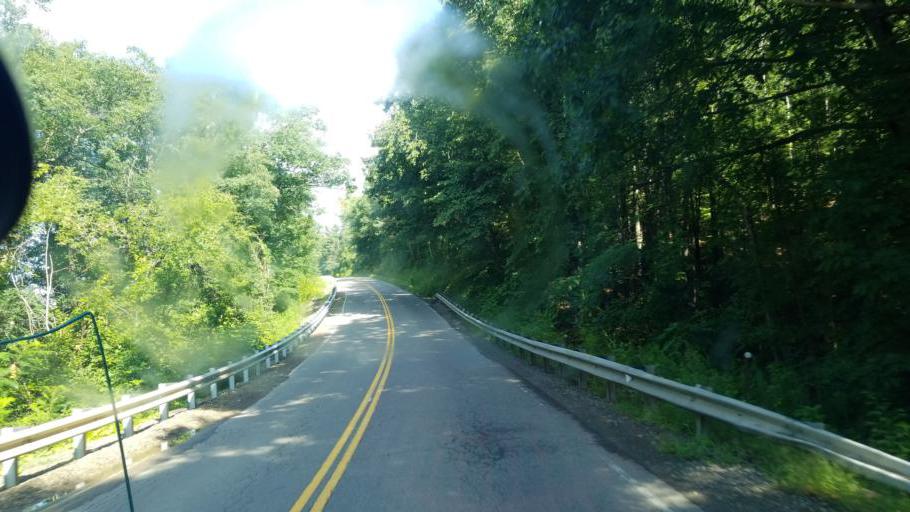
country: US
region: New York
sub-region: Steuben County
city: Canisteo
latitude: 42.2682
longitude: -77.5873
